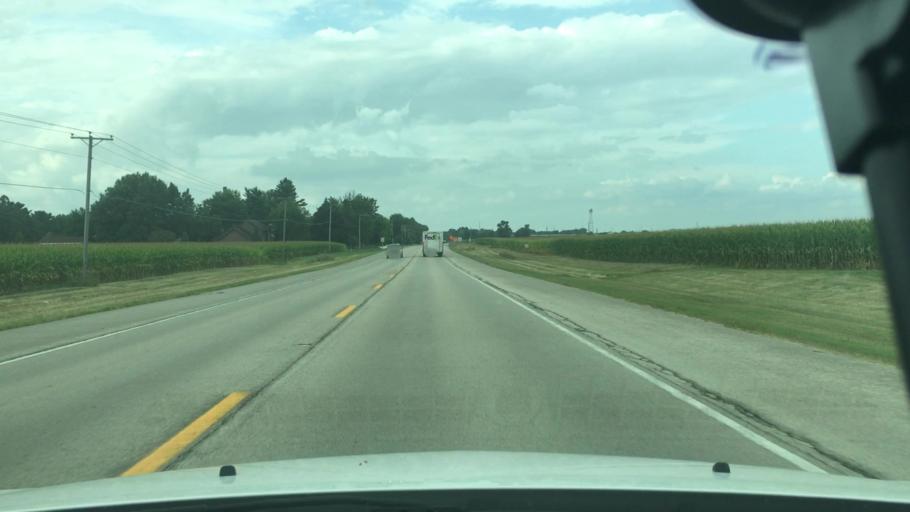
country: US
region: Illinois
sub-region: DeKalb County
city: DeKalb
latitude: 41.8879
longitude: -88.7538
